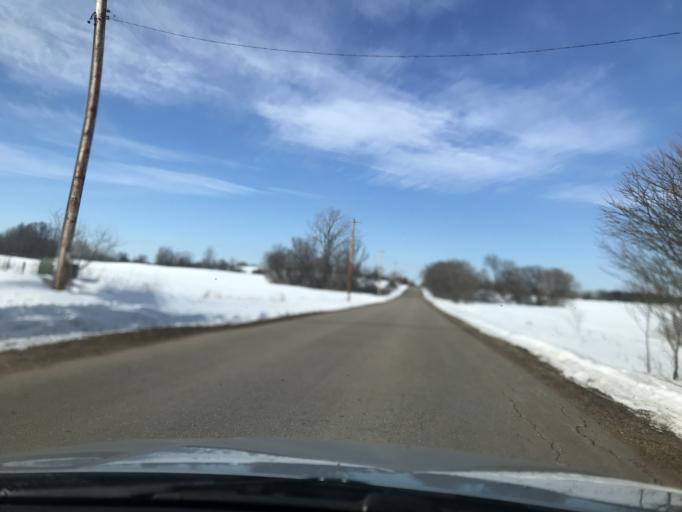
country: US
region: Wisconsin
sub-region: Oconto County
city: Gillett
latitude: 44.9692
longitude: -88.3159
